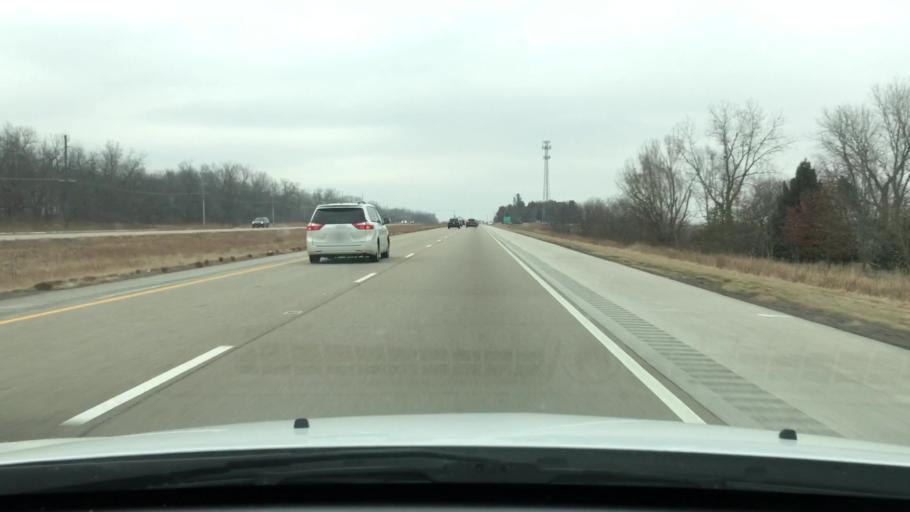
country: US
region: Illinois
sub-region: Logan County
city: Atlanta
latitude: 40.2412
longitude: -89.2537
